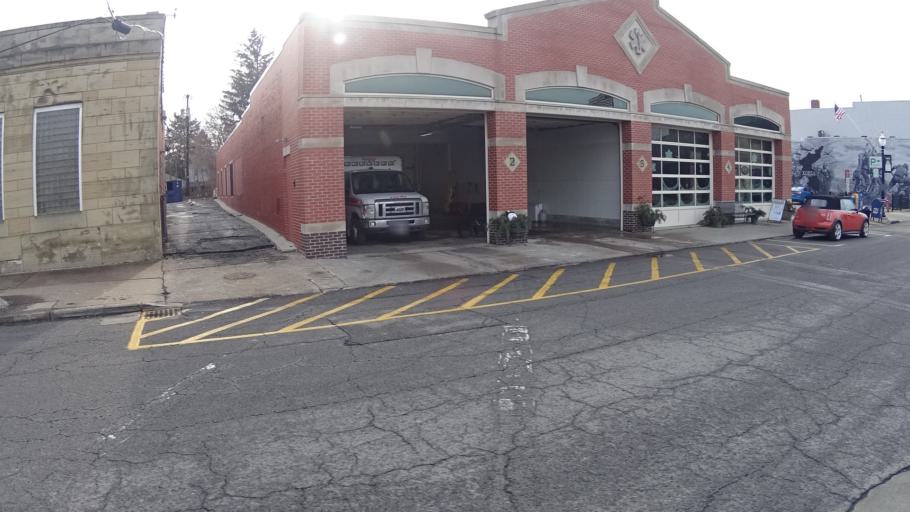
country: US
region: Ohio
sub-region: Lorain County
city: Amherst
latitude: 41.3983
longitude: -82.2239
